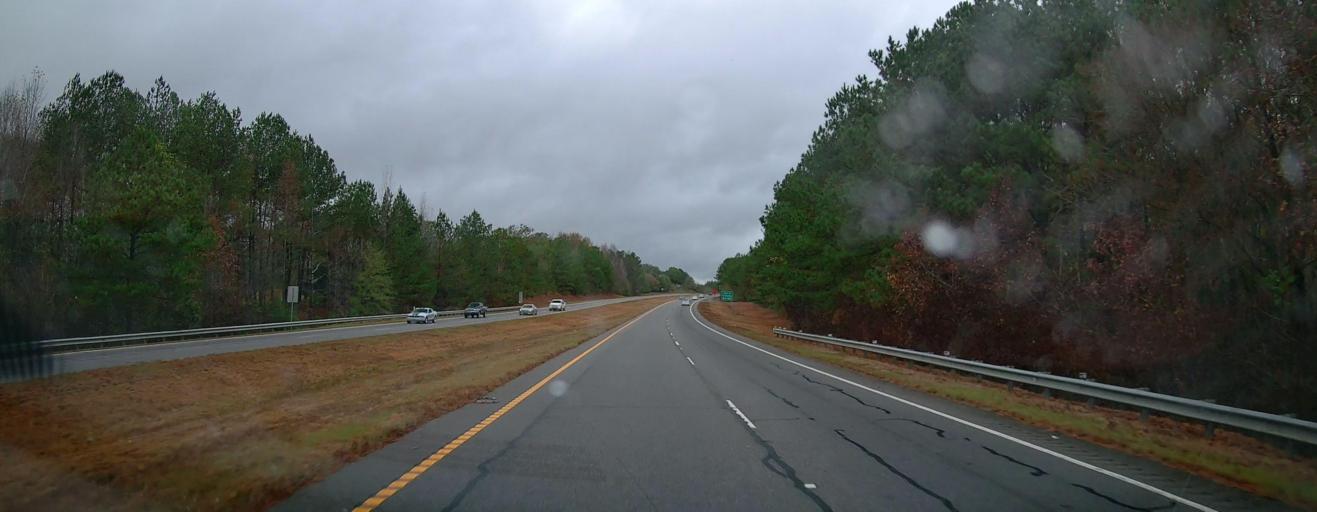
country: US
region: Georgia
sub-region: Oconee County
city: Watkinsville
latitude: 33.8607
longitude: -83.4249
